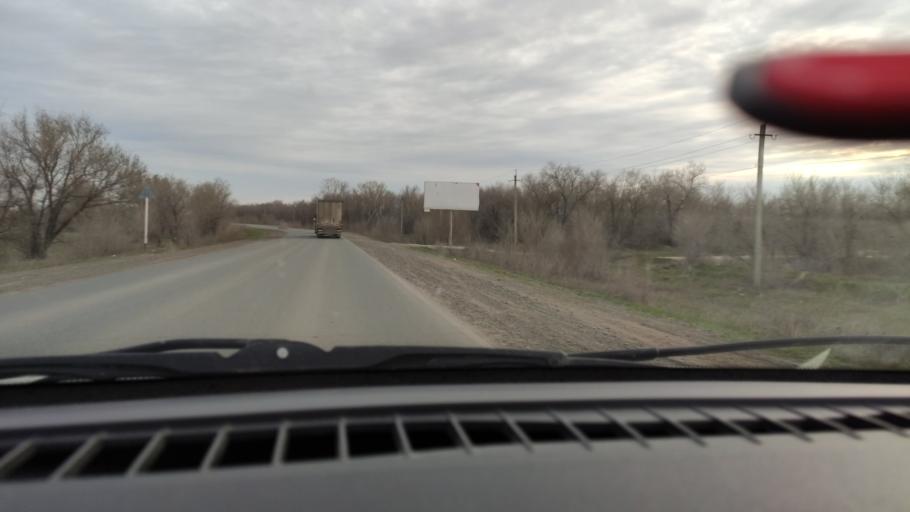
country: RU
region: Orenburg
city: Tatarskaya Kargala
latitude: 51.8961
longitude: 55.1610
